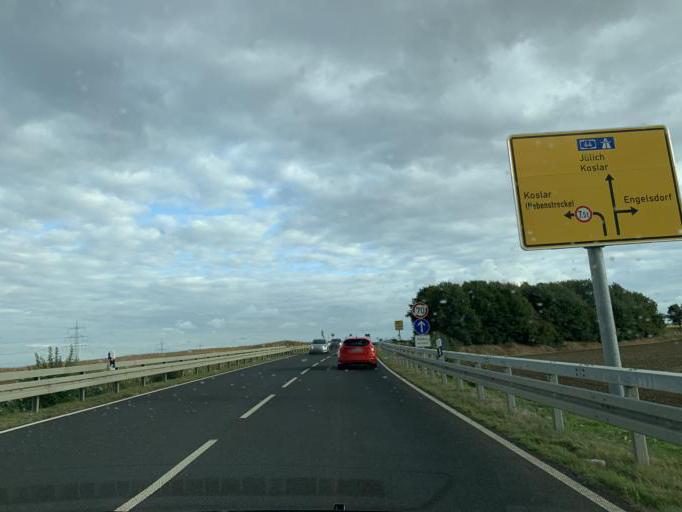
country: DE
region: North Rhine-Westphalia
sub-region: Regierungsbezirk Koln
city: Aldenhoven
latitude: 50.9232
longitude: 6.3078
